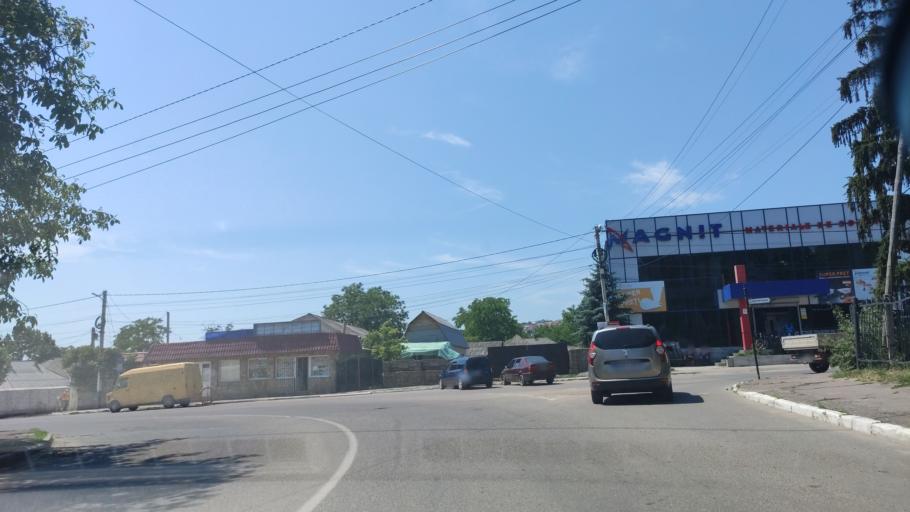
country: MD
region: Raionul Soroca
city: Soroca
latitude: 48.1673
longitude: 28.3035
